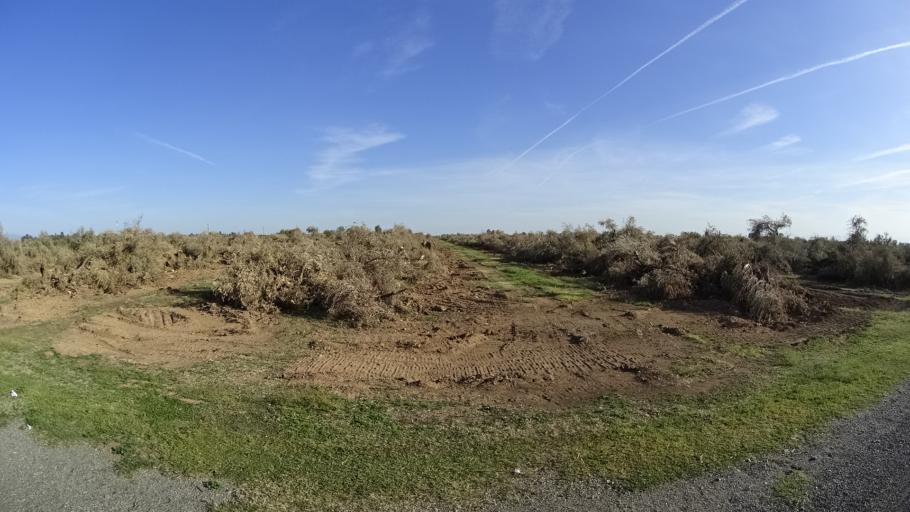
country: US
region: California
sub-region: Glenn County
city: Orland
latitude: 39.7261
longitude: -122.2331
